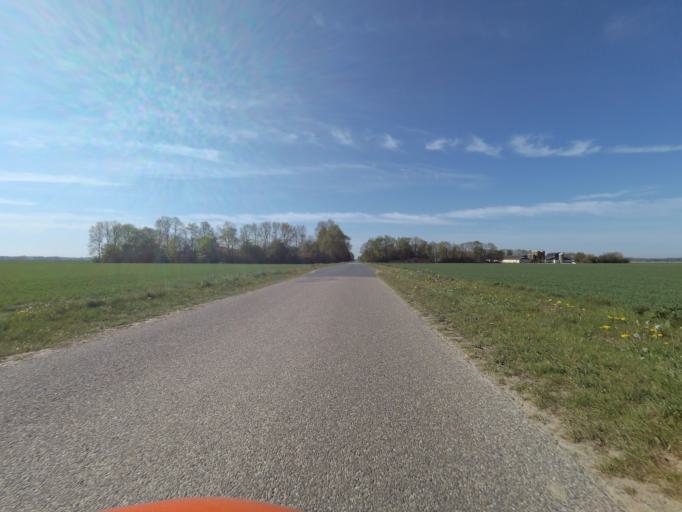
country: NL
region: Flevoland
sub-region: Gemeente Dronten
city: Dronten
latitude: 52.5811
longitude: 5.7041
